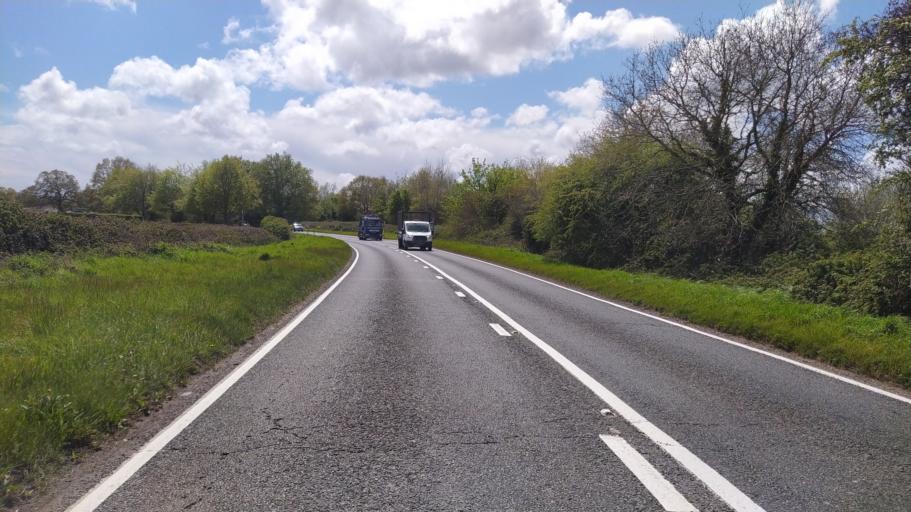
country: GB
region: England
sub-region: Hampshire
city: Fordingbridge
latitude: 50.9003
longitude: -1.7817
